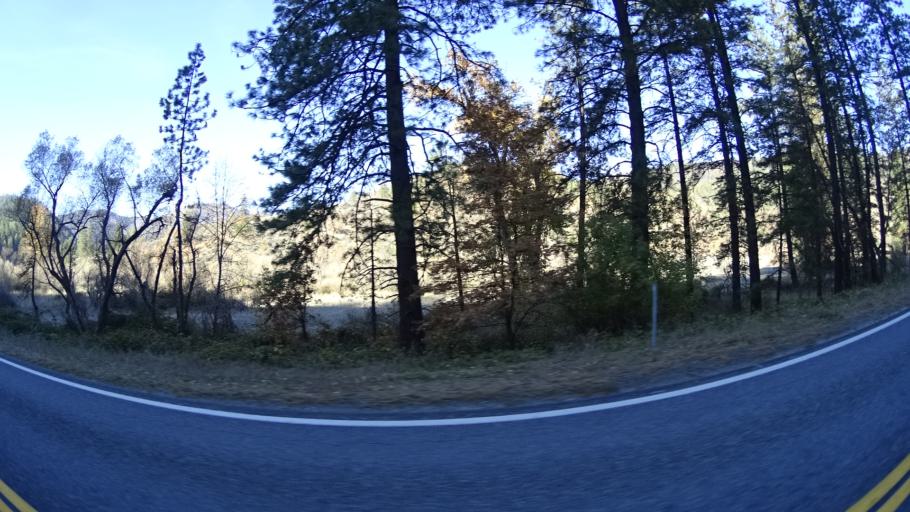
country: US
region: California
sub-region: Siskiyou County
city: Yreka
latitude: 41.8257
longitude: -122.9827
